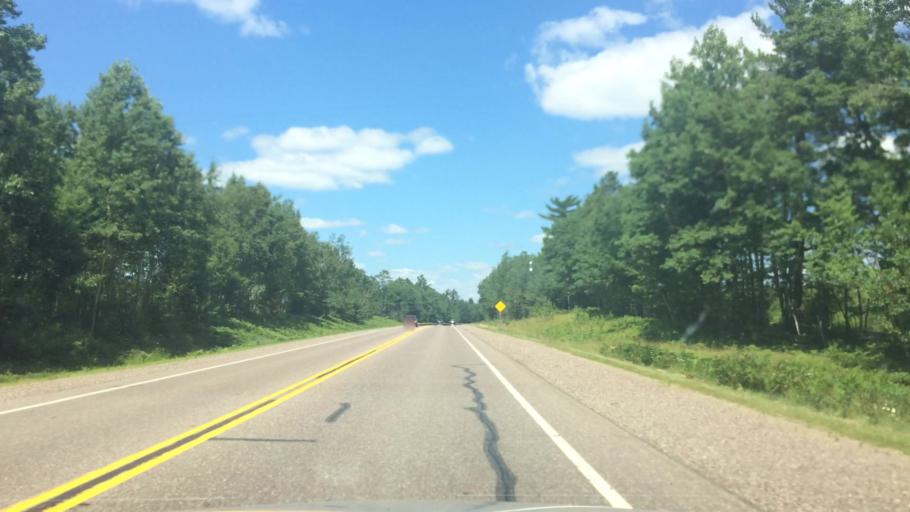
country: US
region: Wisconsin
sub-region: Vilas County
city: Lac du Flambeau
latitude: 45.9441
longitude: -89.6978
